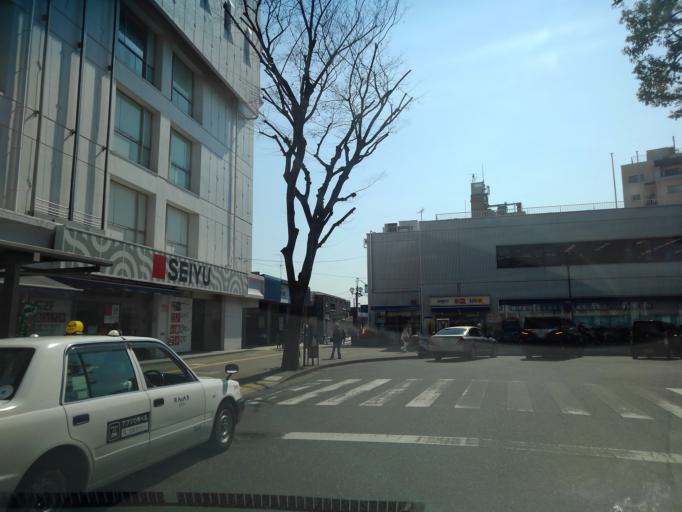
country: JP
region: Saitama
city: Tokorozawa
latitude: 35.8065
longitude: 139.4556
